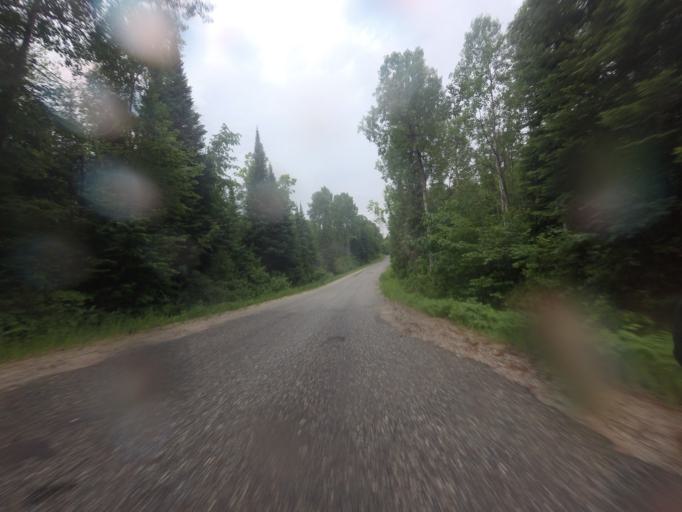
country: CA
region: Quebec
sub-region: Outaouais
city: Maniwaki
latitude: 46.4331
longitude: -75.9456
